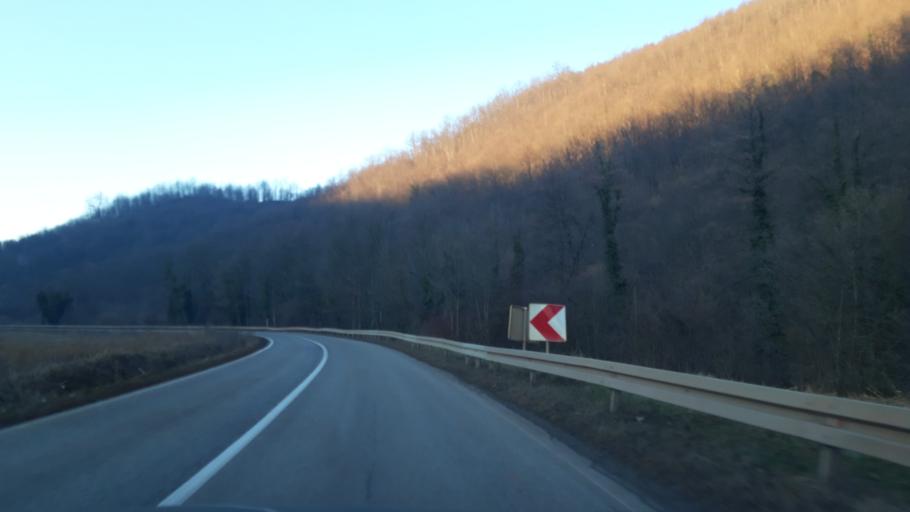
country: BA
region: Republika Srpska
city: Milici
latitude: 44.1854
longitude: 19.0768
